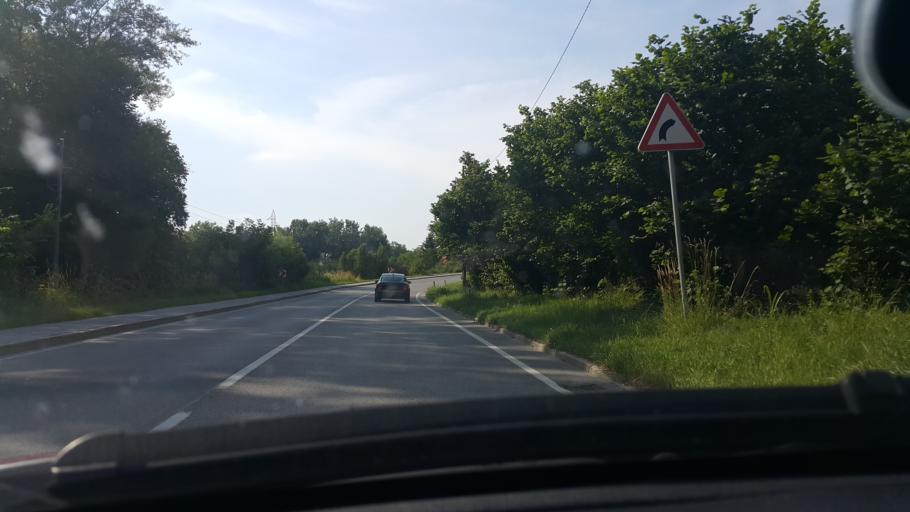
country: SI
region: Duplek
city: Zgornji Duplek
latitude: 46.5107
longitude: 15.7202
